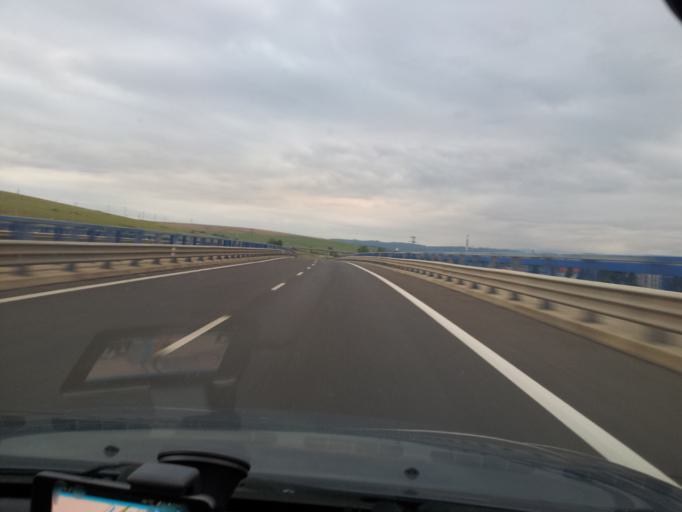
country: SK
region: Presovsky
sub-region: Okres Poprad
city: Poprad
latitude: 49.0826
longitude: 20.3325
